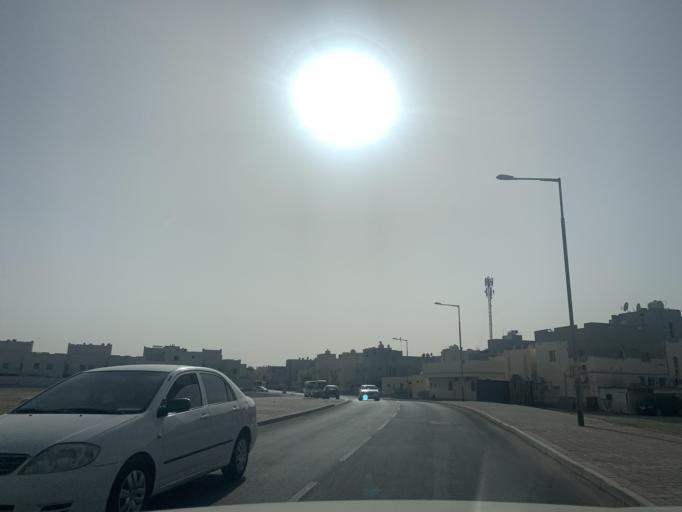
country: BH
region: Northern
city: Sitrah
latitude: 26.1611
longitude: 50.6260
